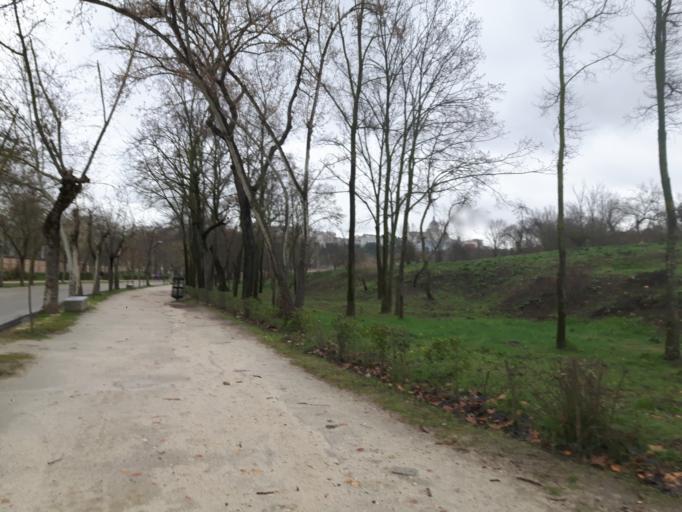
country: ES
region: Madrid
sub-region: Provincia de Madrid
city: Moncloa-Aravaca
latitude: 40.4183
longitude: -3.7279
